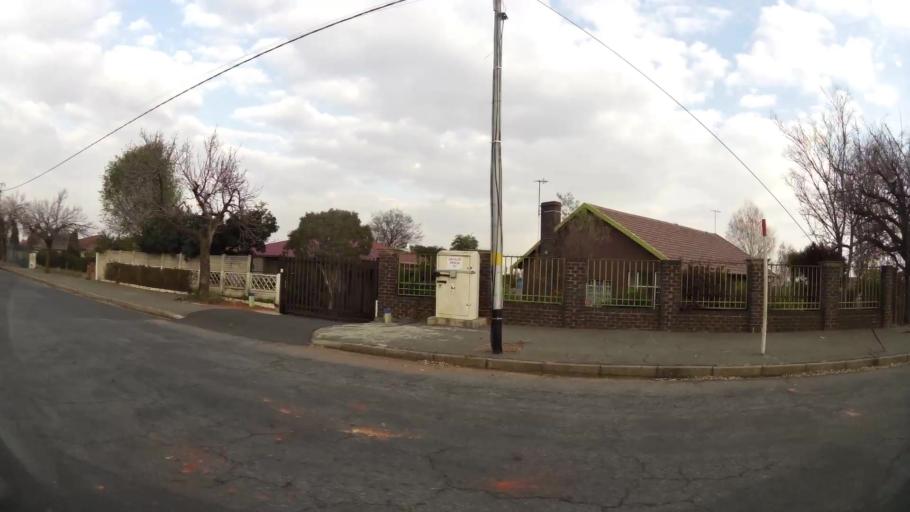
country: ZA
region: Gauteng
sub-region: Ekurhuleni Metropolitan Municipality
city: Germiston
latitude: -26.1774
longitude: 28.1730
